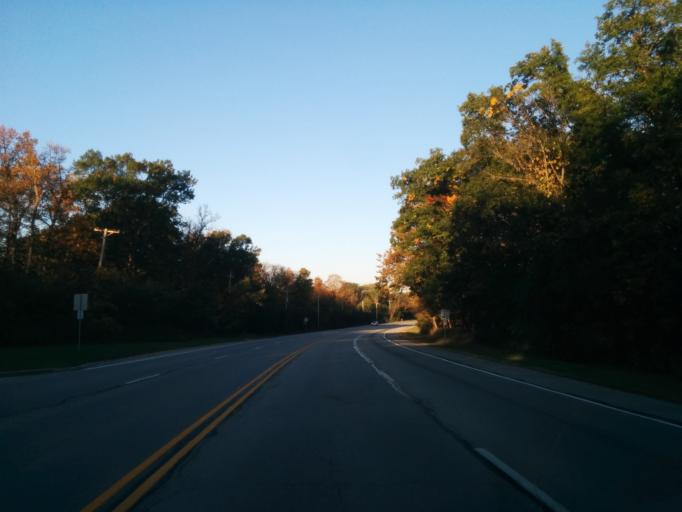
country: US
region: Illinois
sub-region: DuPage County
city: Glen Ellyn
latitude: 41.8889
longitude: -88.0426
